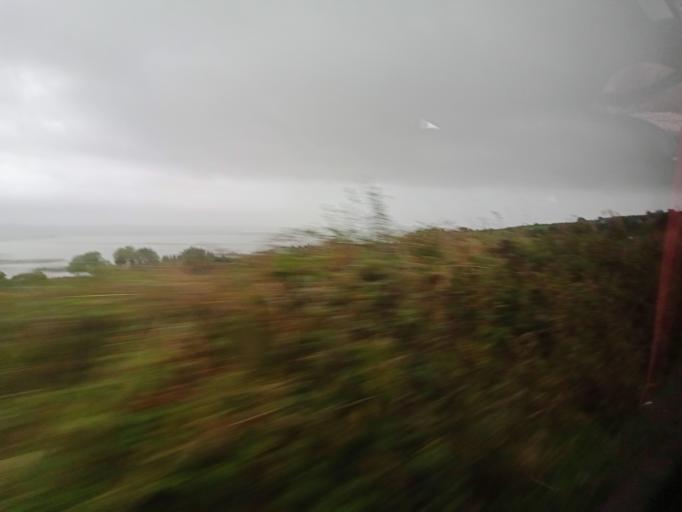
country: IE
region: Munster
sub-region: Waterford
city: Dungarvan
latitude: 52.0501
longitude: -7.6477
